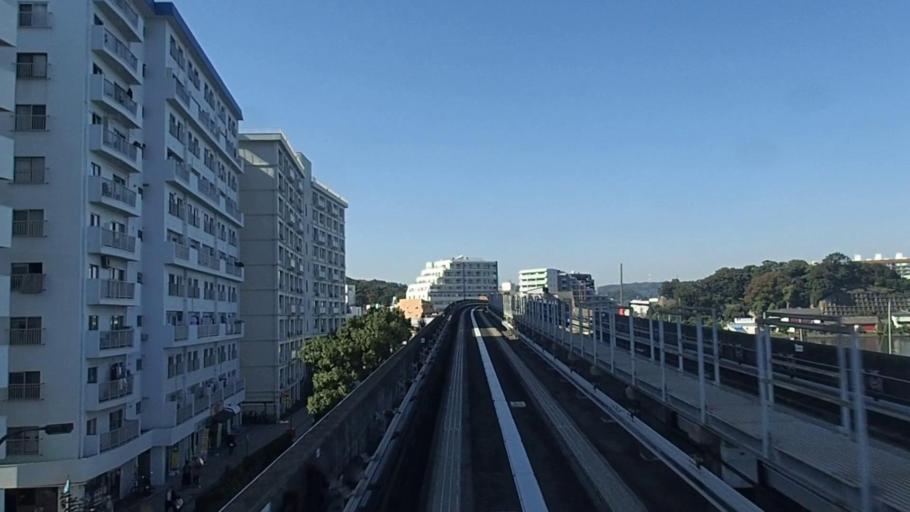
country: JP
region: Kanagawa
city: Zushi
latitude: 35.3294
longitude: 139.6243
